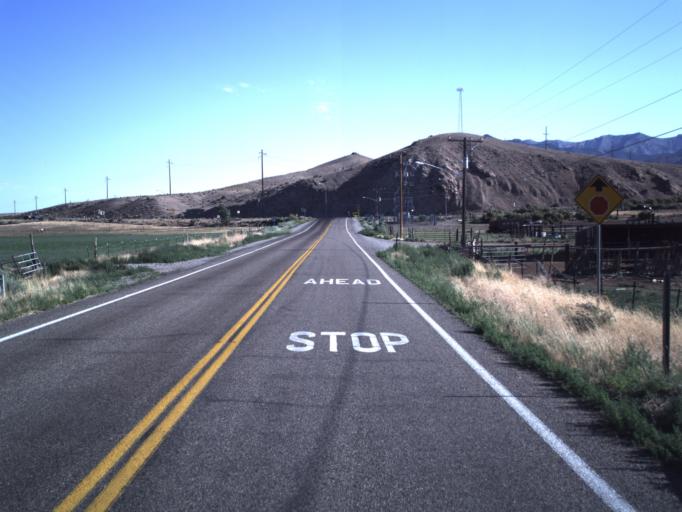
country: US
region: Utah
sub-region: Beaver County
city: Milford
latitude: 38.2176
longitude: -112.9240
